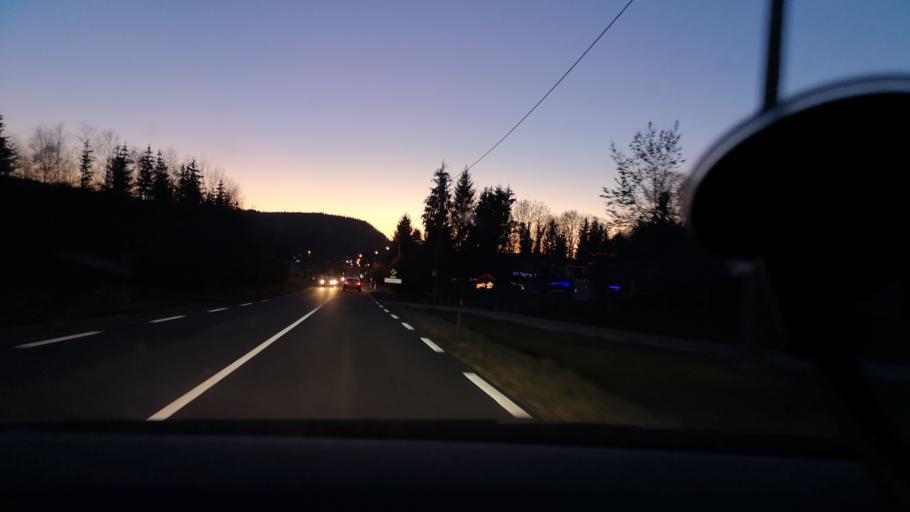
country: FR
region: Franche-Comte
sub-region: Departement du Jura
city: Champagnole
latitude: 46.7497
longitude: 5.9273
